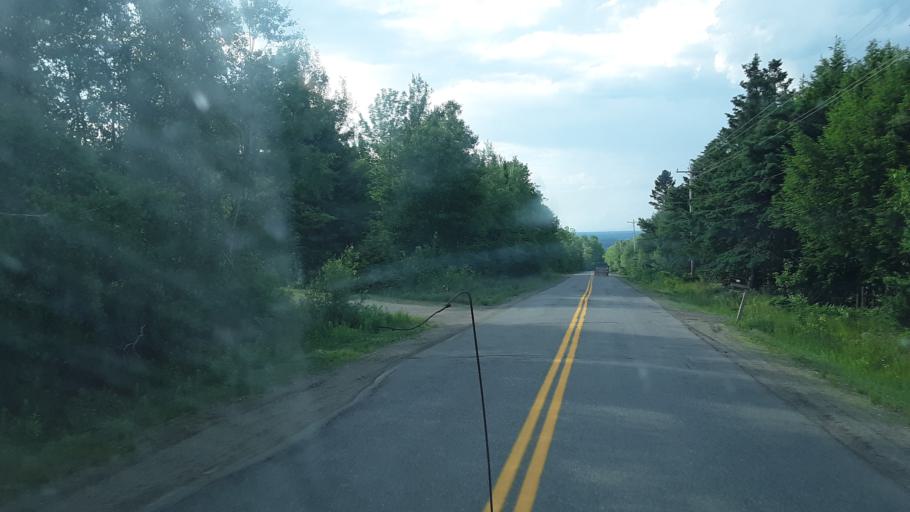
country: US
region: Maine
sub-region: Washington County
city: Calais
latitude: 45.0981
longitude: -67.5094
